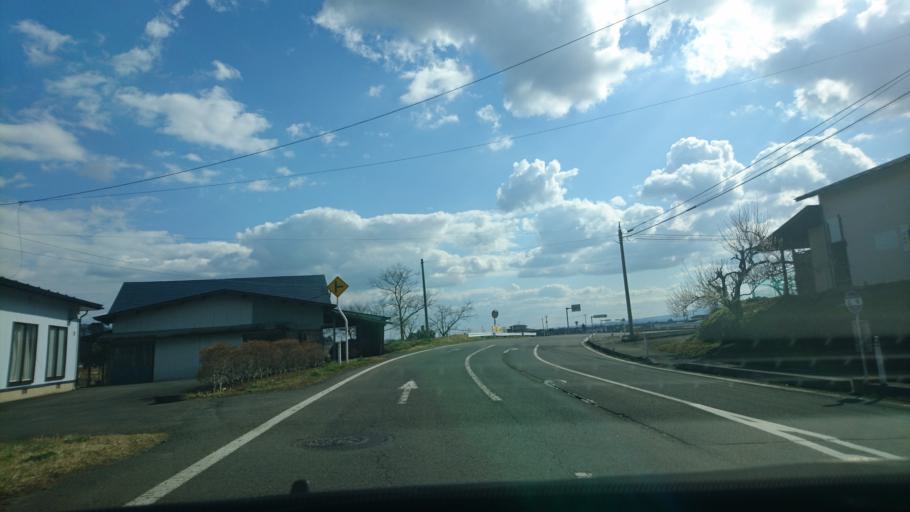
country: JP
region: Iwate
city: Kitakami
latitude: 39.2132
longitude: 141.1619
